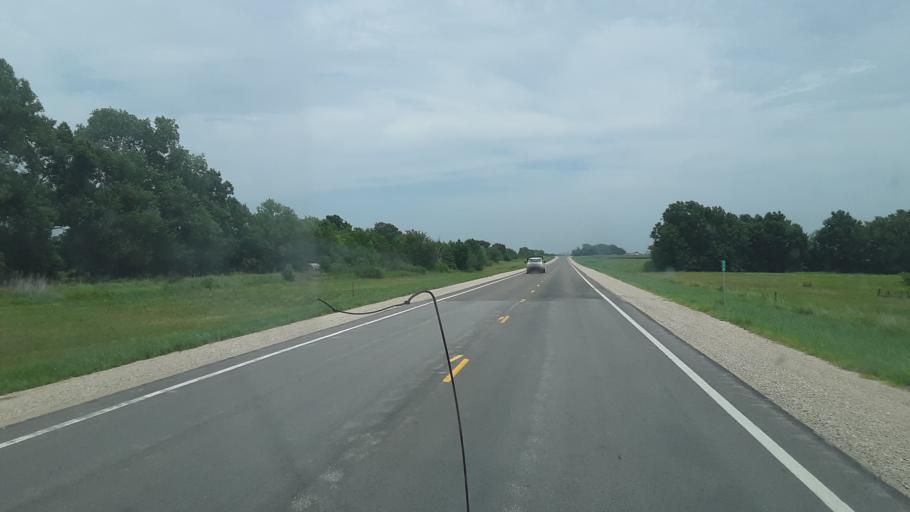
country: US
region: Kansas
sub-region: Woodson County
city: Yates Center
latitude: 37.9118
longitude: -95.5842
